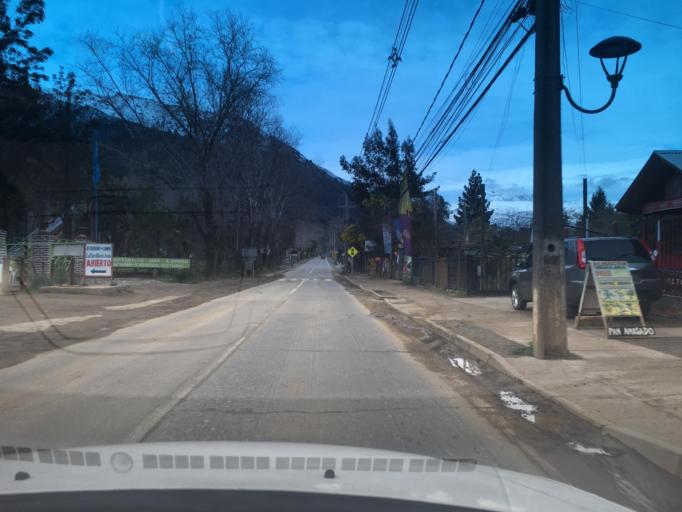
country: CL
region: Santiago Metropolitan
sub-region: Provincia de Cordillera
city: Puente Alto
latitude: -33.5772
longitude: -70.4562
